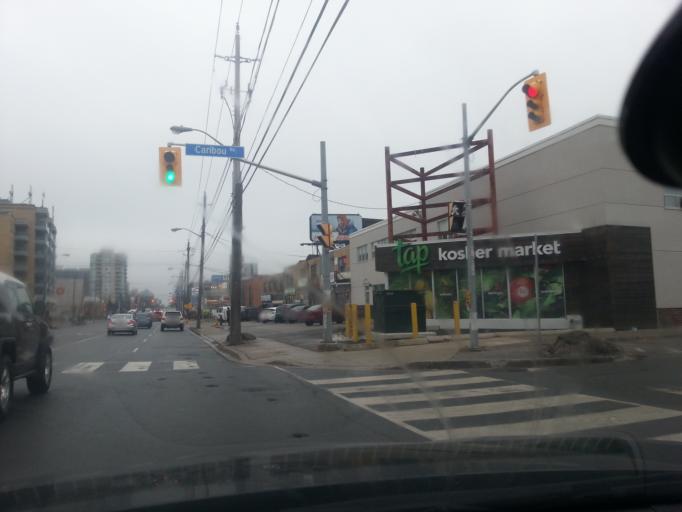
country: CA
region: Ontario
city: Toronto
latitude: 43.7176
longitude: -79.4293
